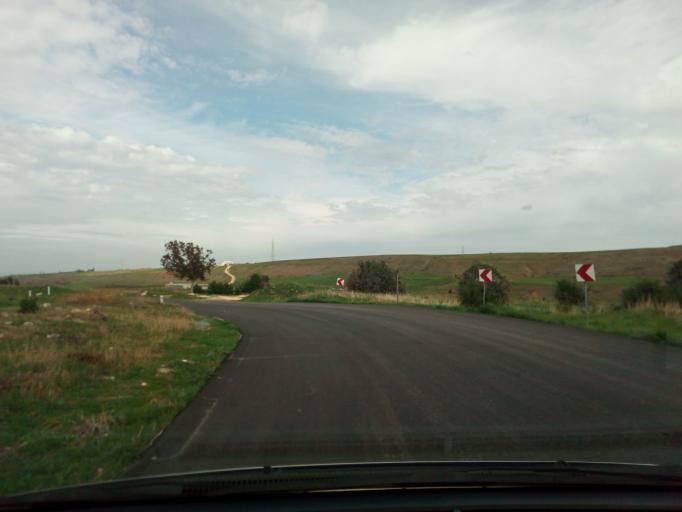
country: CY
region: Lefkosia
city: Astromeritis
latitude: 35.0927
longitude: 32.9937
